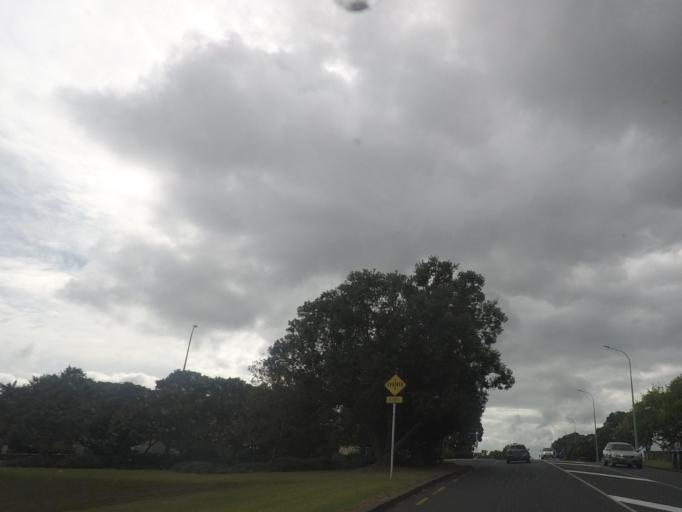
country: NZ
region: Auckland
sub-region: Auckland
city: Tamaki
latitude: -36.8613
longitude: 174.8197
